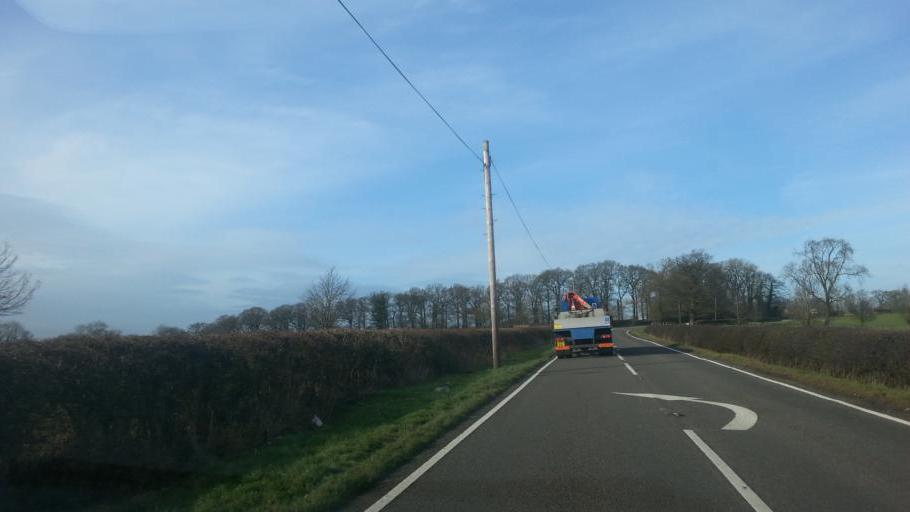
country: GB
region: England
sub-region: Leicestershire
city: Houghton on the Hill
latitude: 52.6700
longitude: -0.9329
